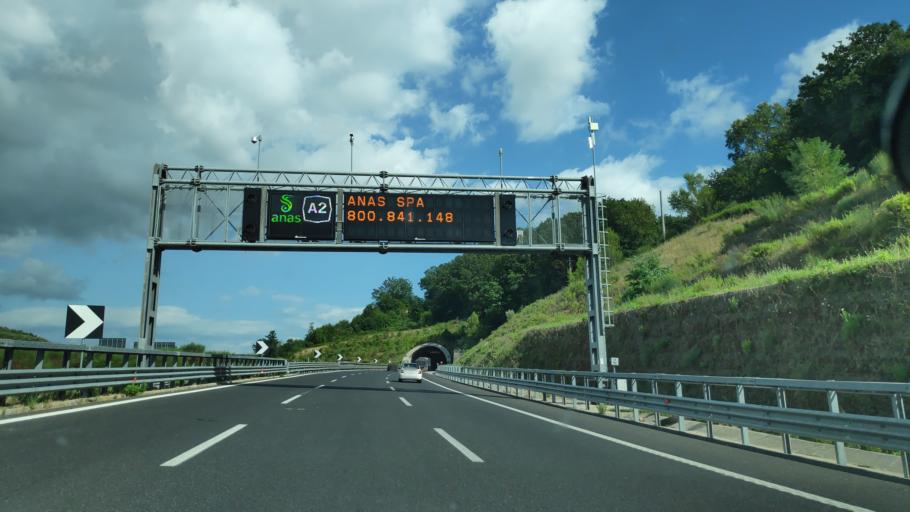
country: IT
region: Campania
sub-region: Provincia di Salerno
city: Contursi Terme
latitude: 40.6276
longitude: 15.2350
